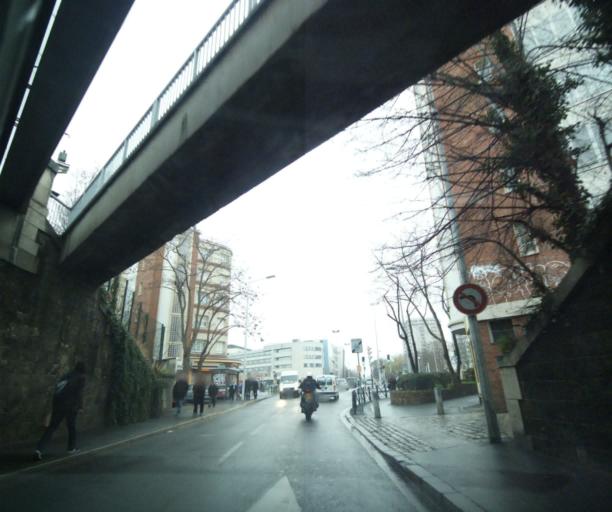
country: FR
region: Ile-de-France
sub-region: Departement des Hauts-de-Seine
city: Nanterre
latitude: 48.8945
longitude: 2.1934
